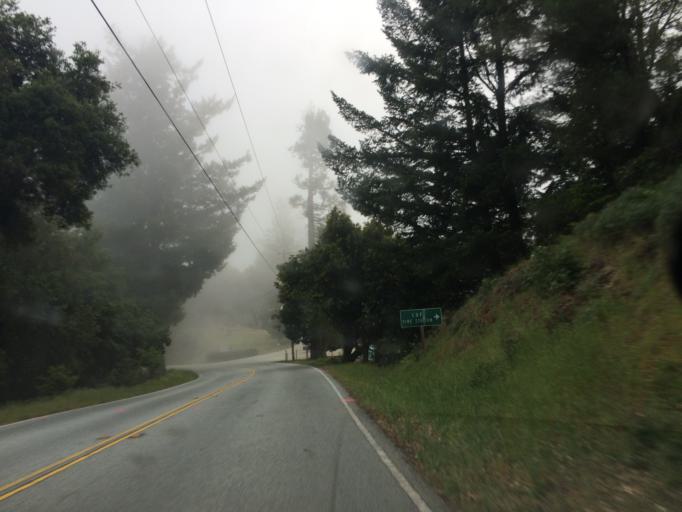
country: US
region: California
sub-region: Santa Clara County
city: Loyola
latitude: 37.2619
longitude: -122.1329
